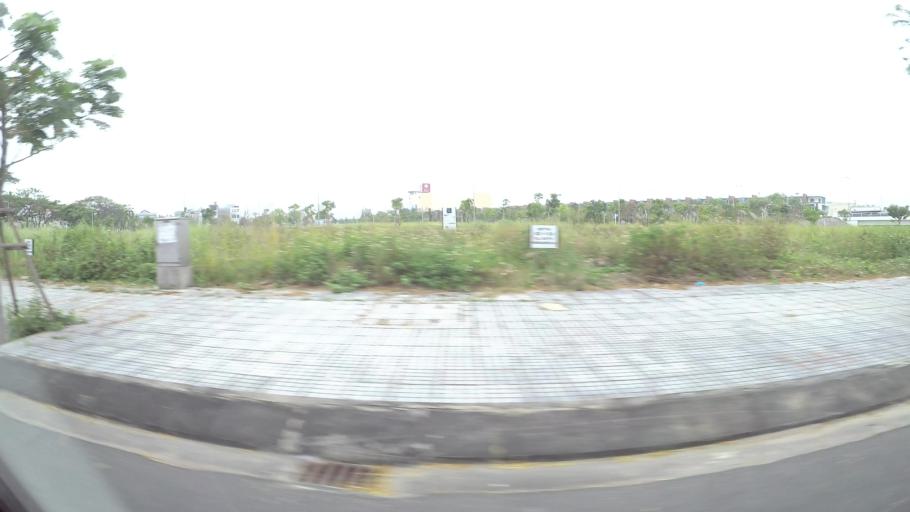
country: VN
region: Da Nang
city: Ngu Hanh Son
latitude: 16.0333
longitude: 108.2337
